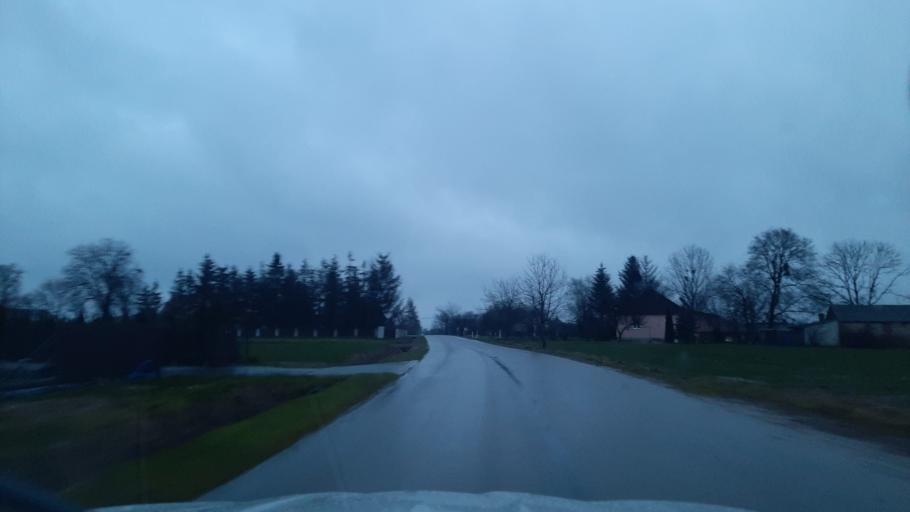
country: PL
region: Lublin Voivodeship
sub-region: Powiat lubelski
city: Jastkow
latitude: 51.3548
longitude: 22.4155
